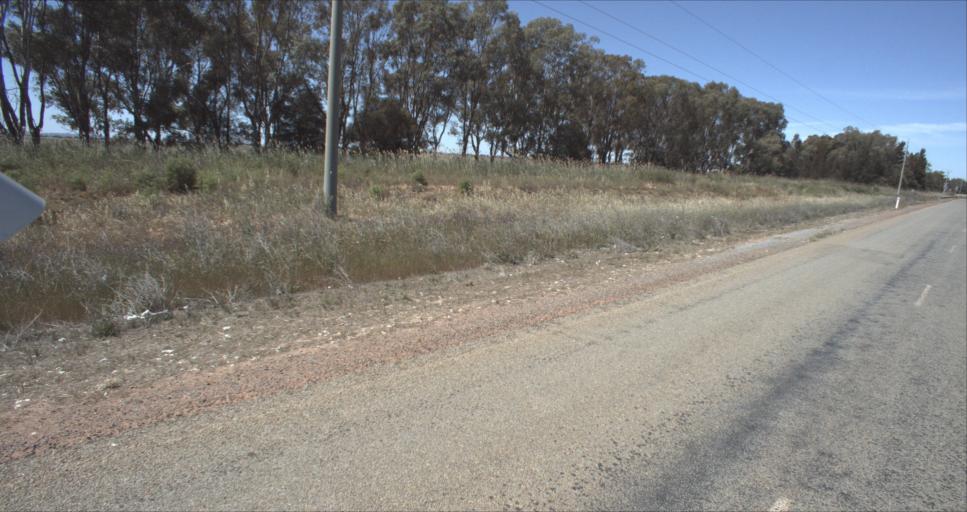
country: AU
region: New South Wales
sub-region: Leeton
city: Leeton
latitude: -34.4635
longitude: 146.2937
